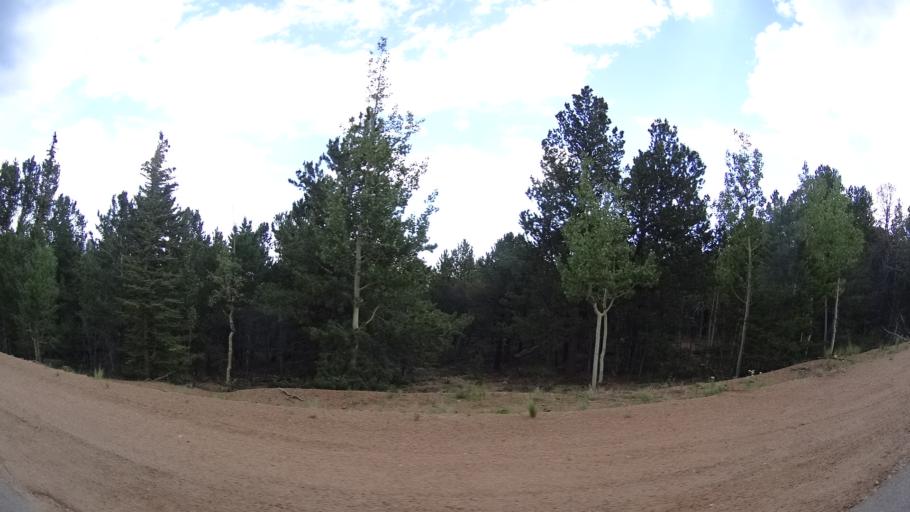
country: US
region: Colorado
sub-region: El Paso County
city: Cascade-Chipita Park
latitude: 38.8981
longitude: -105.0651
